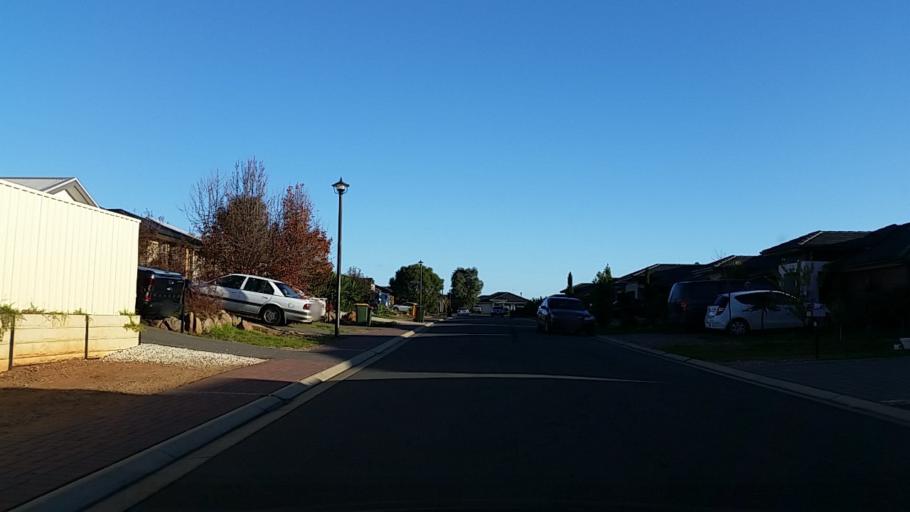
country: AU
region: South Australia
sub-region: Playford
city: Smithfield
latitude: -34.6814
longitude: 138.6843
